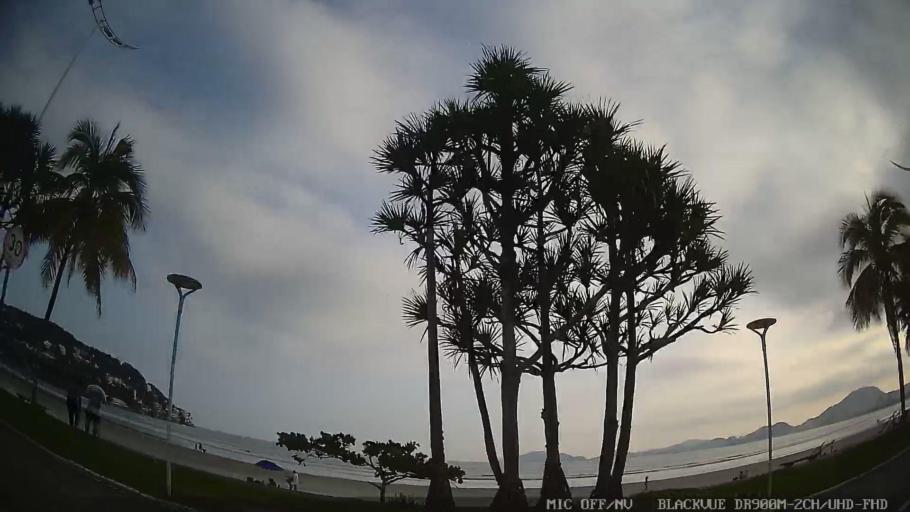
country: BR
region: Sao Paulo
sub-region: Guaruja
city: Guaruja
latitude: -23.9890
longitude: -46.2038
